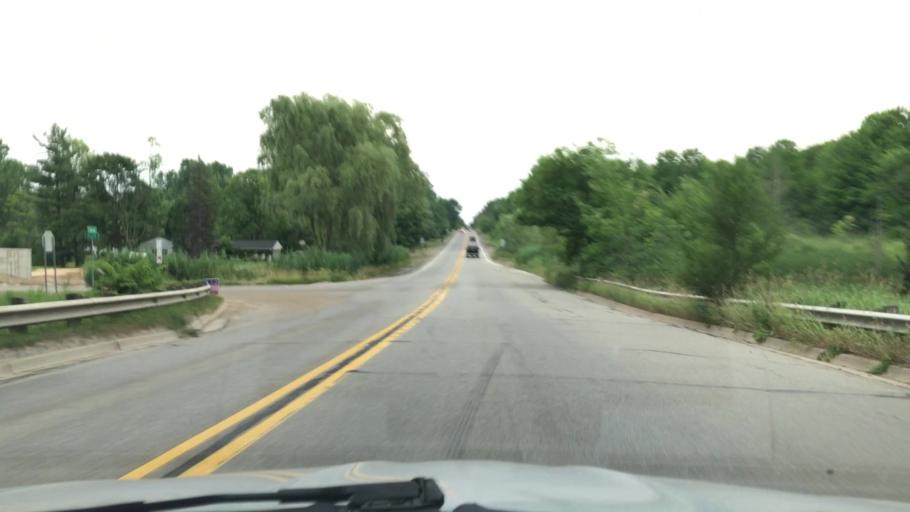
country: US
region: Michigan
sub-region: Wayne County
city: Northville
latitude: 42.4307
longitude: -83.5123
